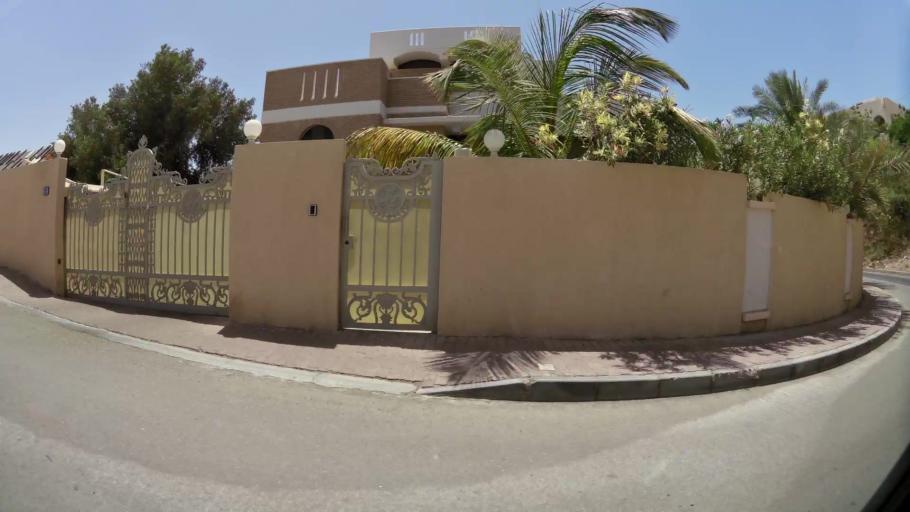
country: OM
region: Muhafazat Masqat
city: Muscat
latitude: 23.6250
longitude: 58.4916
